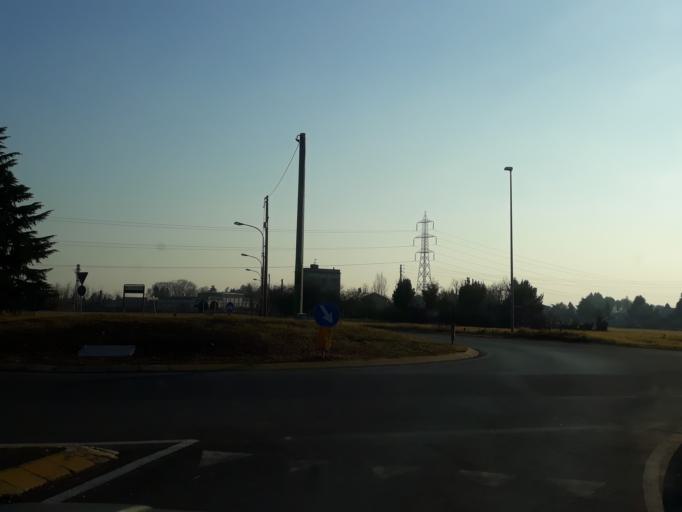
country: IT
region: Lombardy
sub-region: Provincia di Monza e Brianza
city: Bellusco
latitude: 45.6300
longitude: 9.4182
